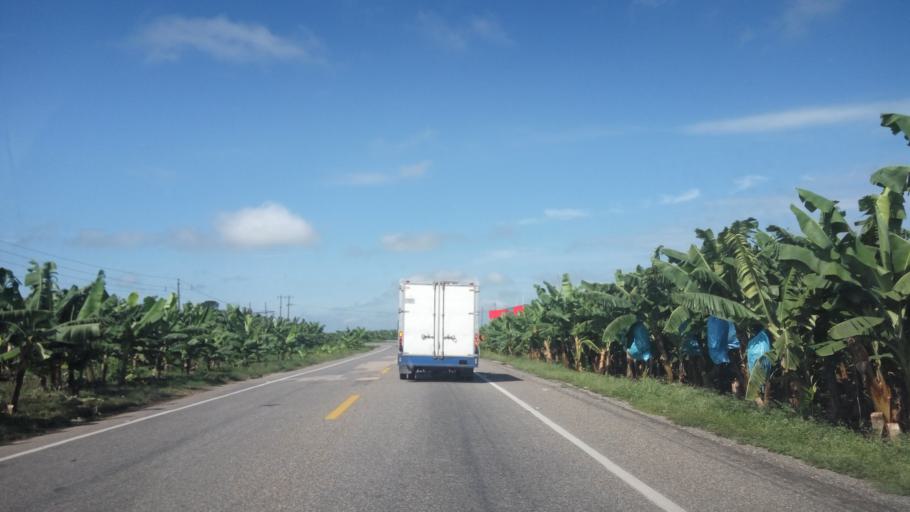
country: MX
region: Tabasco
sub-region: Teapa
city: Eureka y Belen
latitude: 17.6528
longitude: -92.9616
